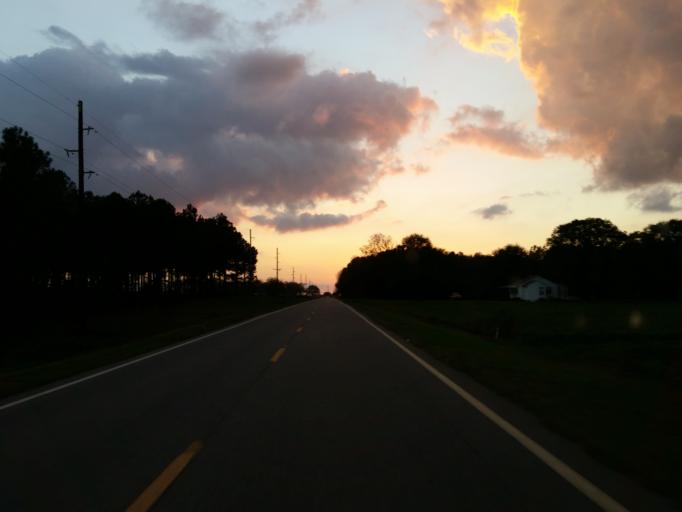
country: US
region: Georgia
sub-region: Dooly County
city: Vienna
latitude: 32.1352
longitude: -83.6907
